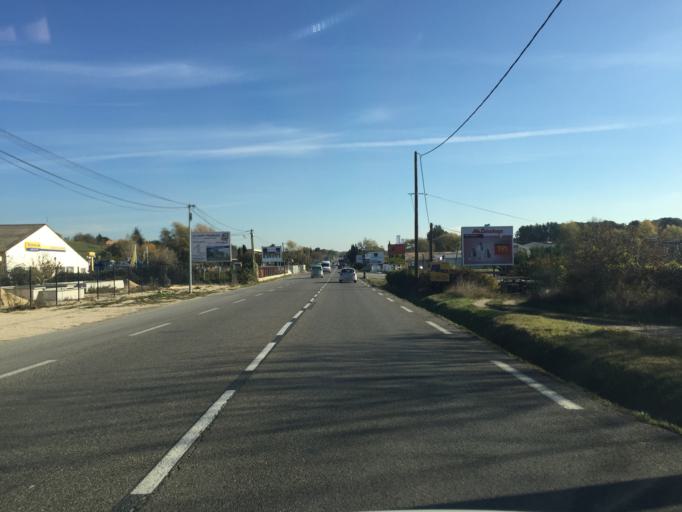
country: FR
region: Provence-Alpes-Cote d'Azur
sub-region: Departement des Bouches-du-Rhone
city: Eguilles
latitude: 43.5833
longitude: 5.3741
